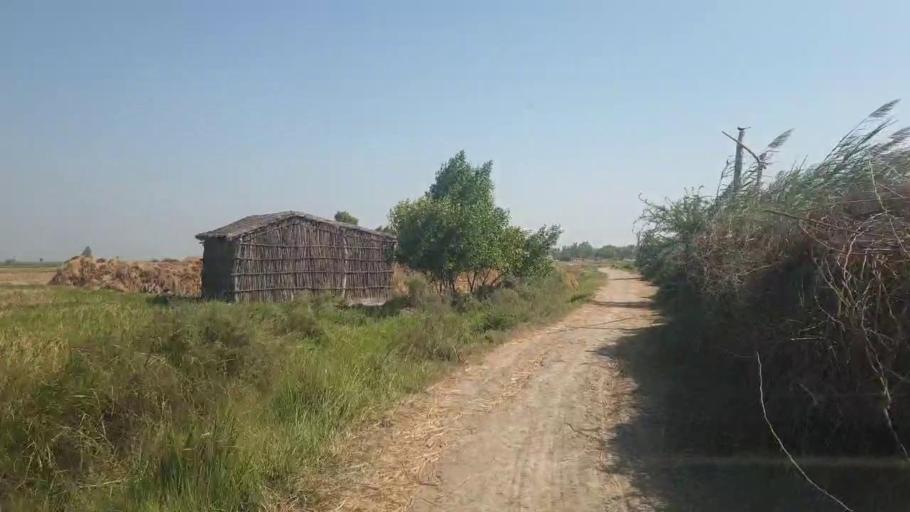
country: PK
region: Sindh
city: Badin
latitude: 24.6810
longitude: 68.8956
